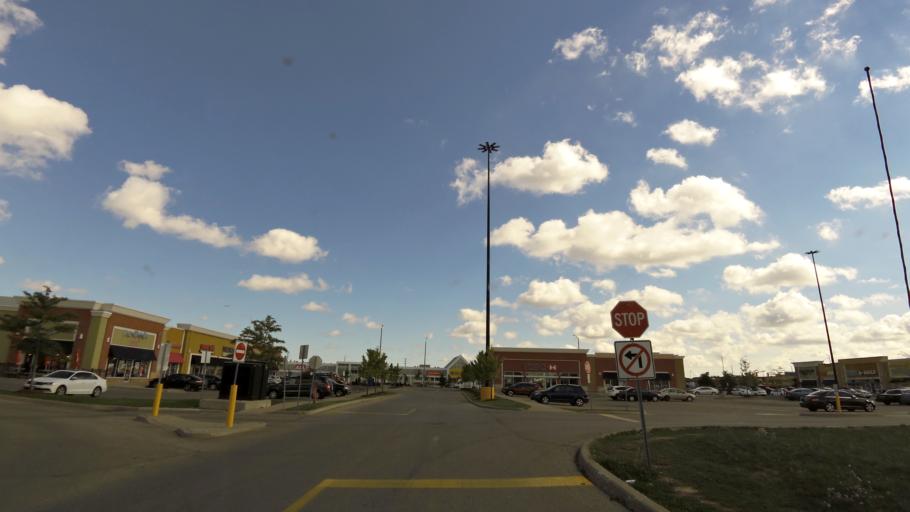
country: CA
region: Ontario
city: Brampton
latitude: 43.5969
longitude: -79.7866
